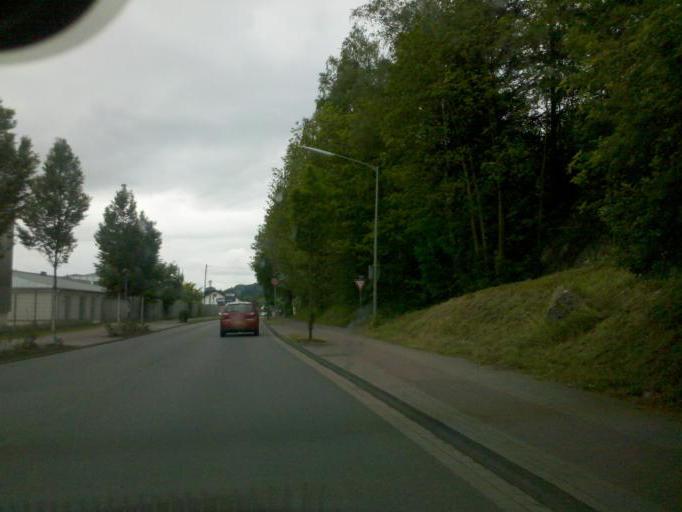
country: DE
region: North Rhine-Westphalia
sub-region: Regierungsbezirk Arnsberg
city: Lennestadt
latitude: 51.1476
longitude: 8.0319
